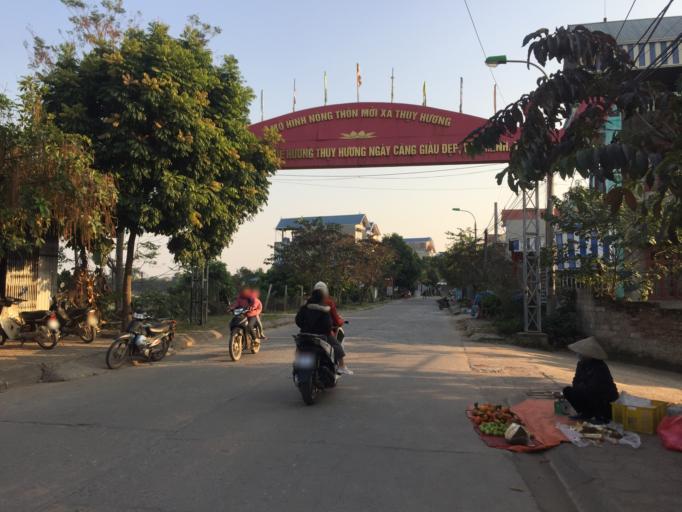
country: VN
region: Ha Noi
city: Chuc Son
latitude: 20.9147
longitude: 105.7140
